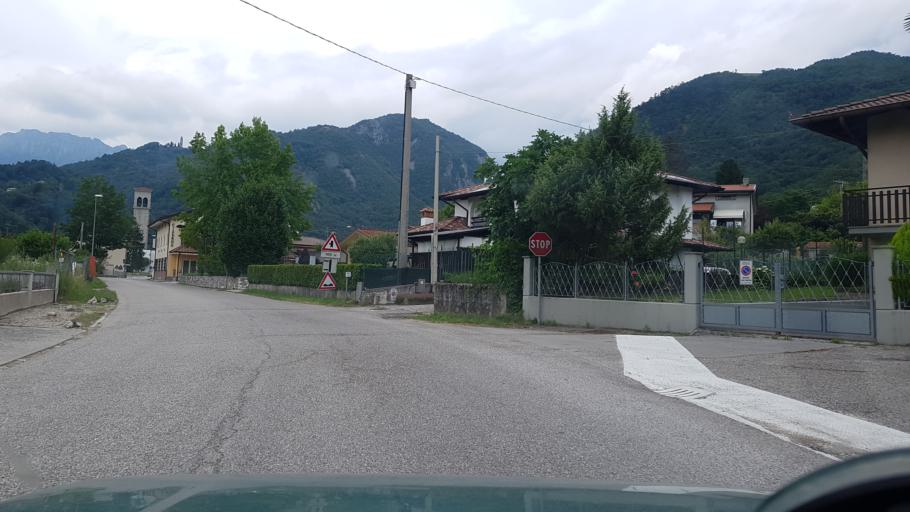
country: IT
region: Friuli Venezia Giulia
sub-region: Provincia di Udine
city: Tarcento
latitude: 46.2286
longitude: 13.2278
